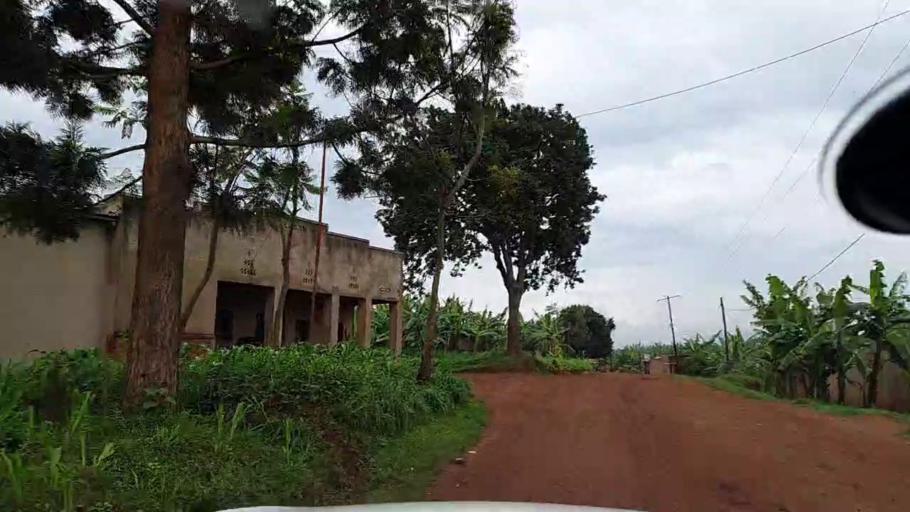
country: RW
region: Kigali
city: Kigali
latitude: -1.9136
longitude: 29.8984
